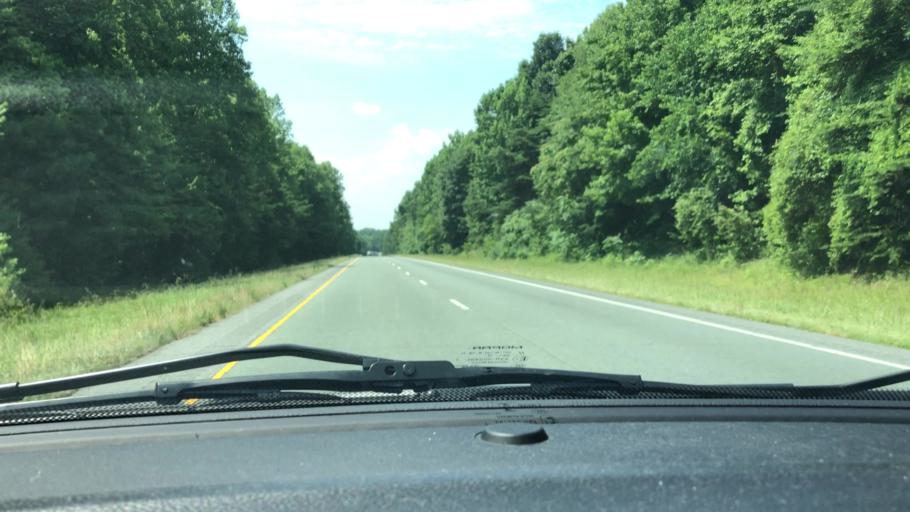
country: US
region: North Carolina
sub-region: Randolph County
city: Liberty
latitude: 35.8570
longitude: -79.6141
